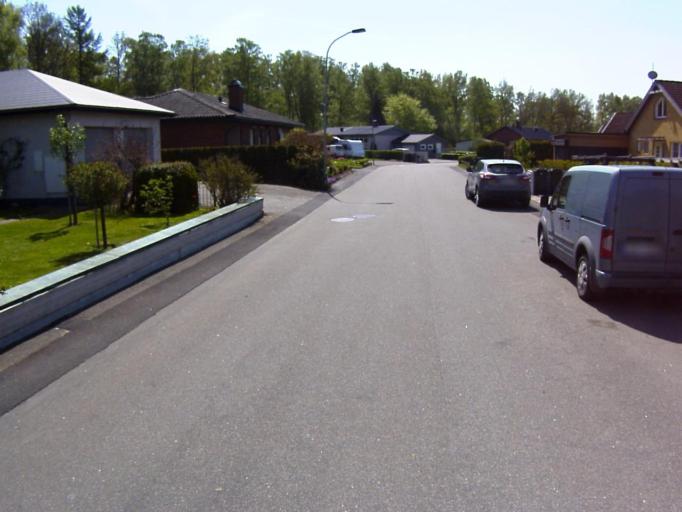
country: SE
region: Skane
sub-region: Kristianstads Kommun
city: Onnestad
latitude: 55.9308
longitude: 13.9890
